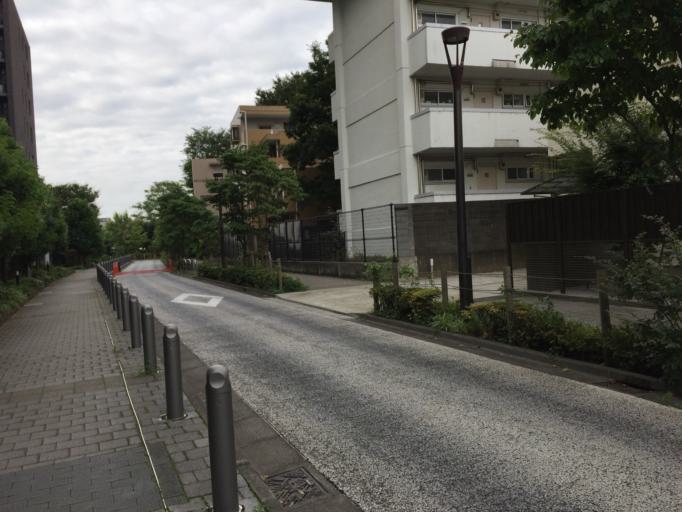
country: JP
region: Tokyo
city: Tokyo
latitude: 35.6509
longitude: 139.6700
